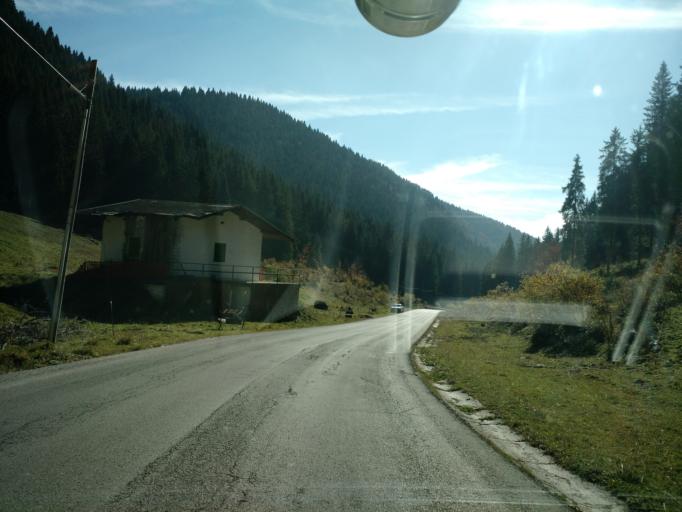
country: IT
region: Veneto
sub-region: Provincia di Vicenza
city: Gallio
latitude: 45.9172
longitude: 11.5647
